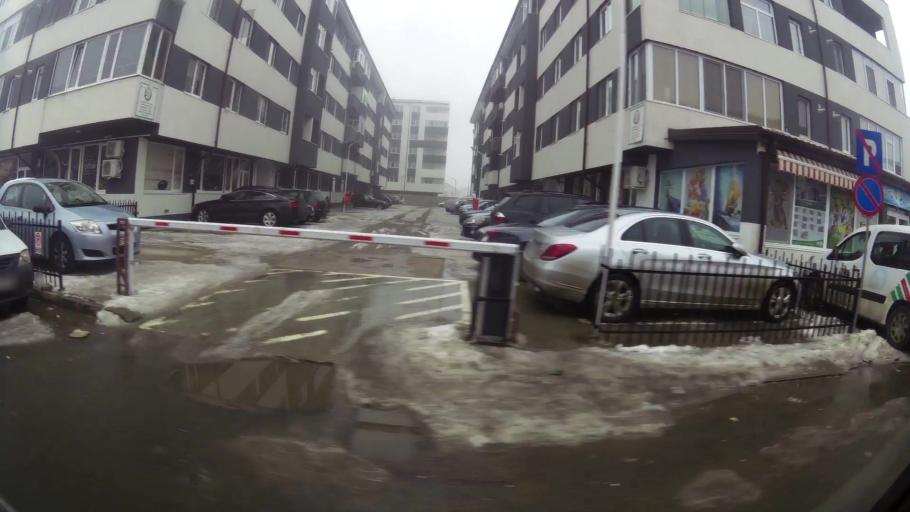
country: RO
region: Ilfov
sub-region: Comuna Chiajna
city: Chiajna
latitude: 44.4534
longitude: 25.9853
